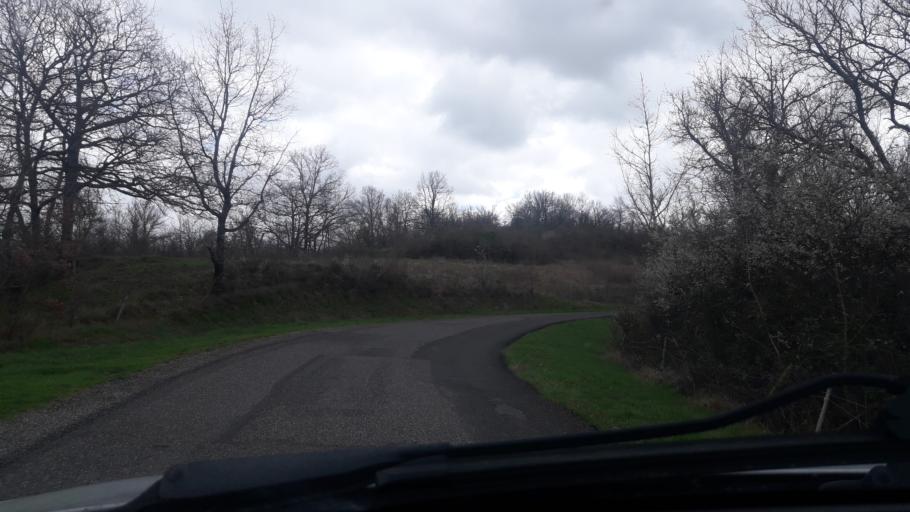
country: FR
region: Midi-Pyrenees
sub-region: Departement de la Haute-Garonne
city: Montesquieu-Volvestre
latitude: 43.2304
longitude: 1.2853
